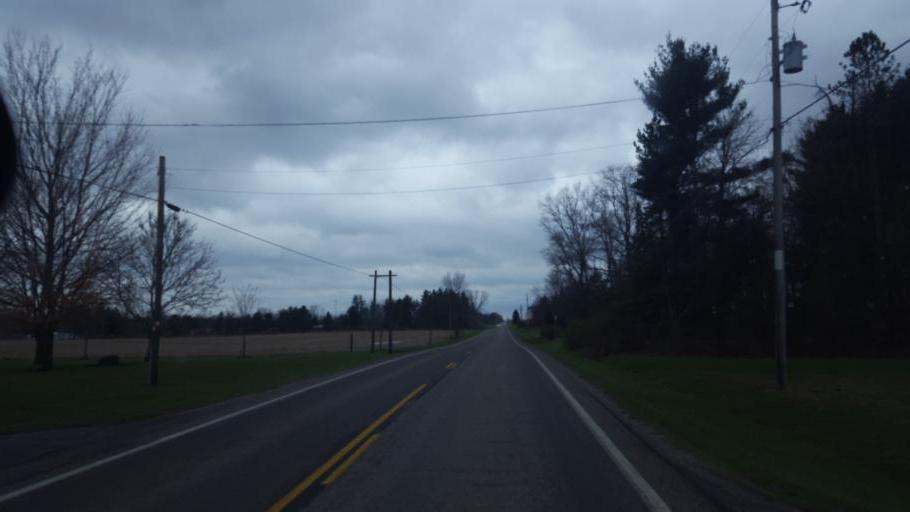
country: US
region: Ohio
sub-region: Morrow County
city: Cardington
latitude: 40.4288
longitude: -82.8248
